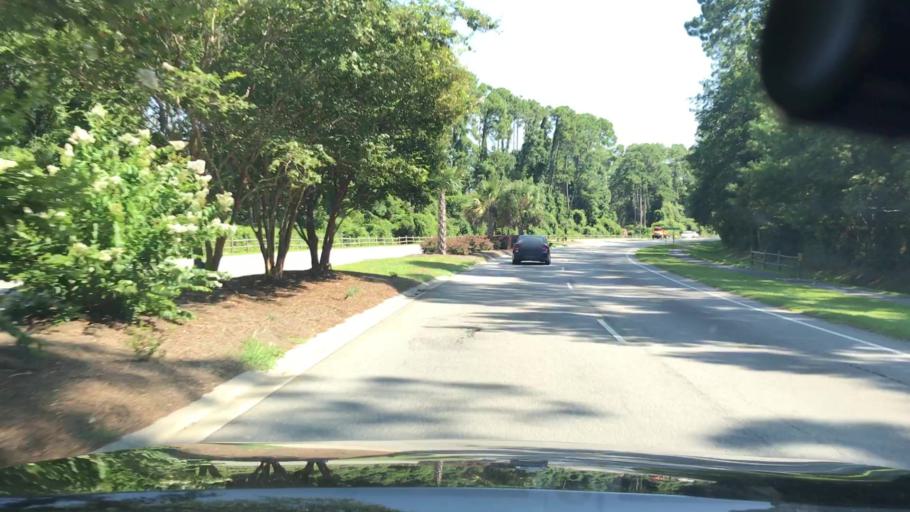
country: US
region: South Carolina
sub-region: Beaufort County
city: Hilton Head Island
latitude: 32.1710
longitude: -80.7737
